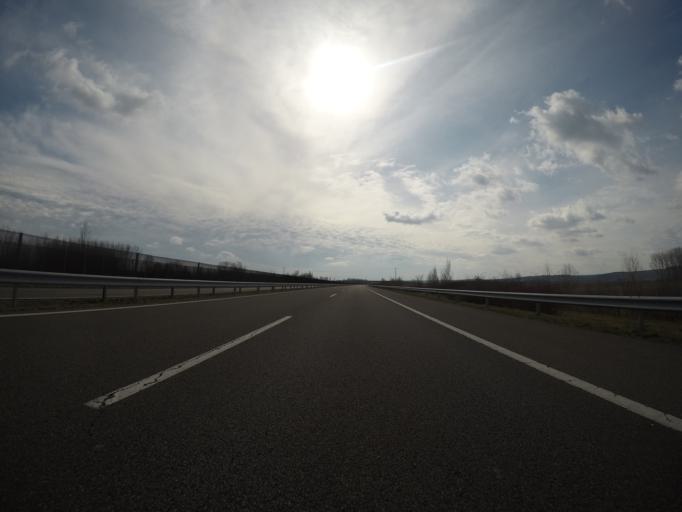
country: HU
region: Tolna
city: Decs
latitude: 46.2511
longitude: 18.7214
